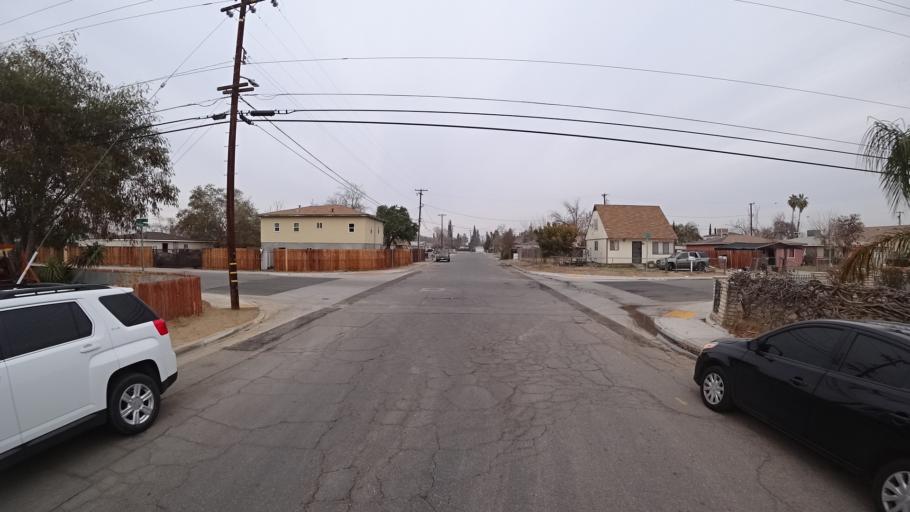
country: US
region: California
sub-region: Kern County
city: Bakersfield
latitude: 35.3591
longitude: -118.9980
